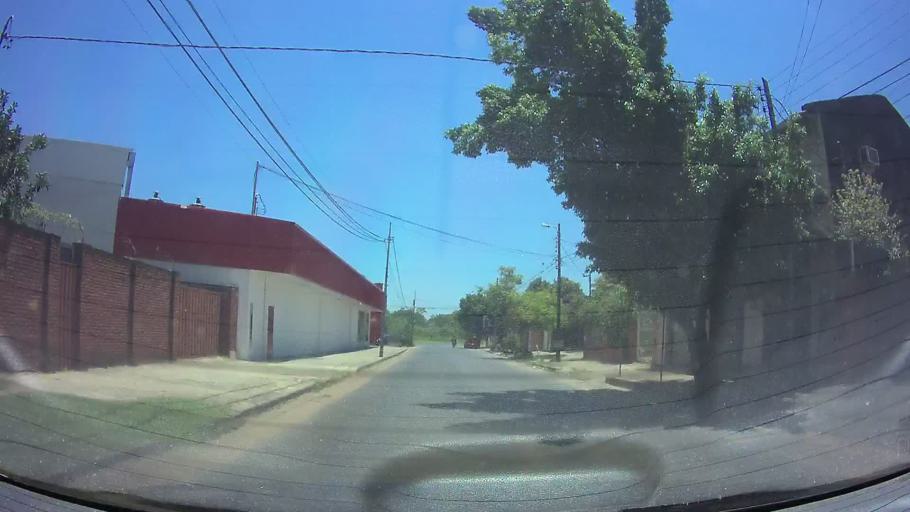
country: PY
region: Central
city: Fernando de la Mora
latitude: -25.2813
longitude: -57.5342
